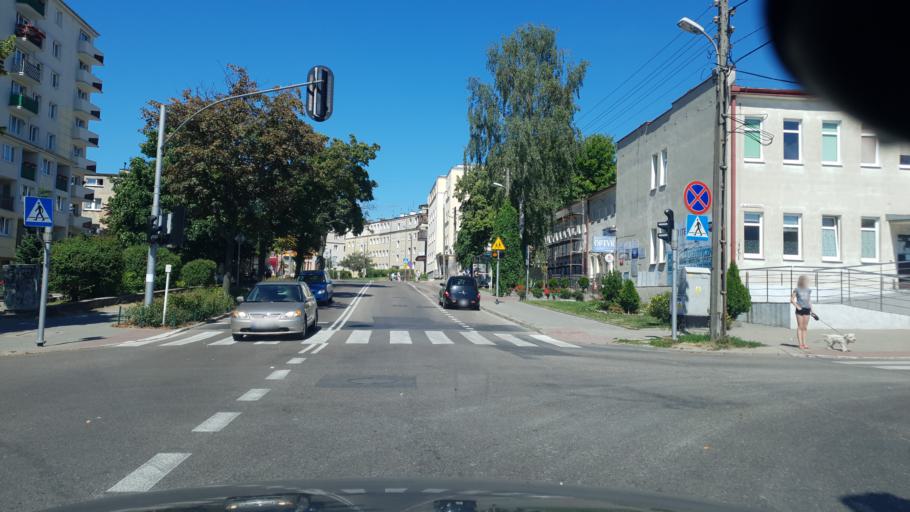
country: PL
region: Pomeranian Voivodeship
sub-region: Gdynia
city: Gdynia
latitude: 54.5028
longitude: 18.5416
